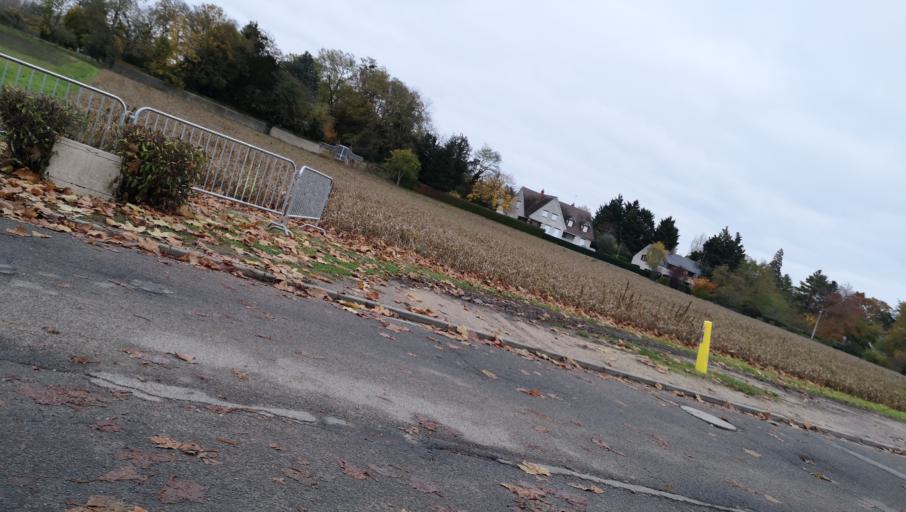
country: FR
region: Centre
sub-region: Departement du Loiret
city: Saint-Jean-de-Braye
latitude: 47.9003
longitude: 1.9867
